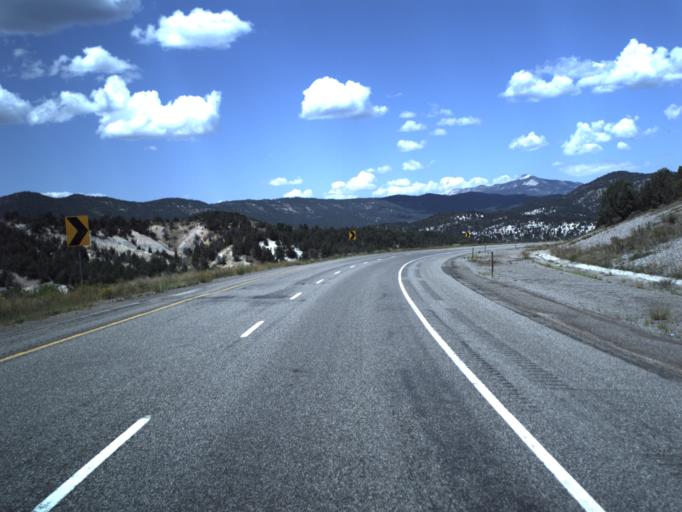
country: US
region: Utah
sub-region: Sevier County
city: Salina
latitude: 38.8594
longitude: -111.5524
